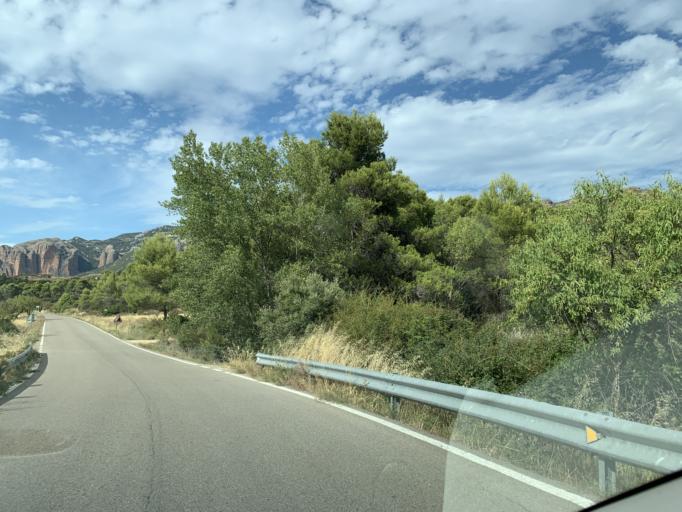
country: ES
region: Aragon
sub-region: Provincia de Zaragoza
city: Santa Eulalia de Gallego
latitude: 42.3199
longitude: -0.7242
